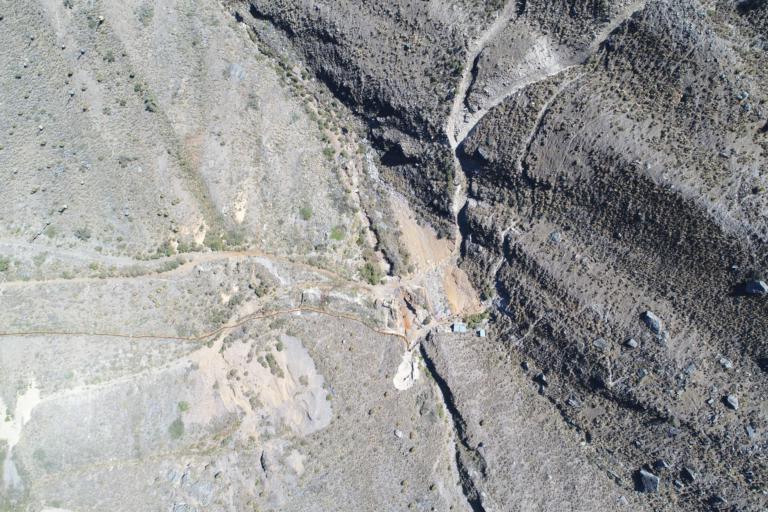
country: BO
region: La Paz
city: Viloco
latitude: -16.8075
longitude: -67.5541
